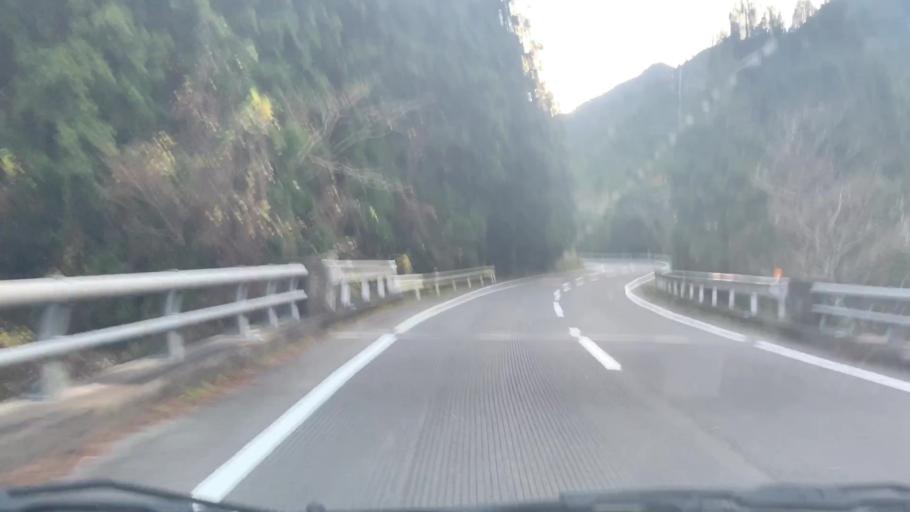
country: JP
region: Saga Prefecture
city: Kashima
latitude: 33.0113
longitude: 130.0634
